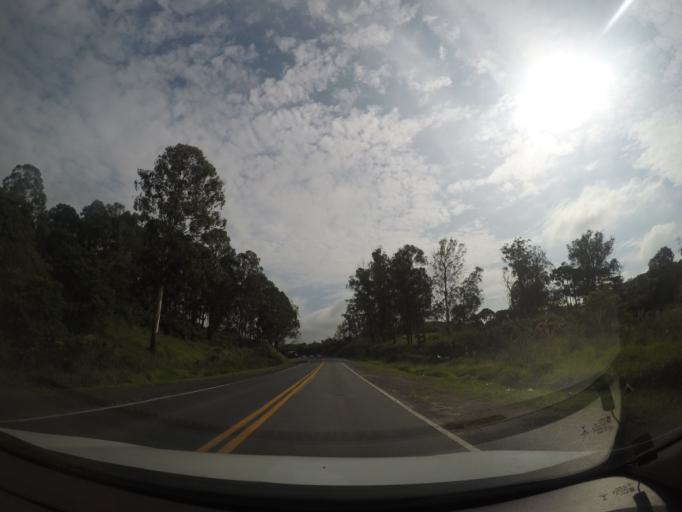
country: BR
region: Parana
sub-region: Colombo
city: Colombo
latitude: -25.3399
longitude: -49.2410
